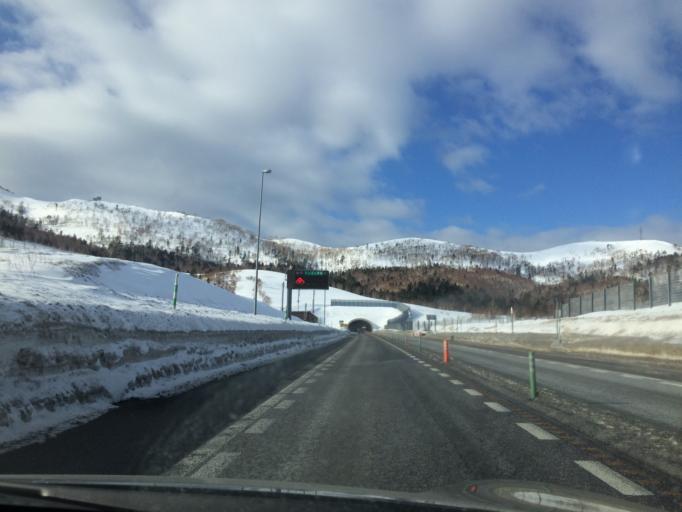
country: JP
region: Hokkaido
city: Shimo-furano
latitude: 43.0588
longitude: 142.7115
